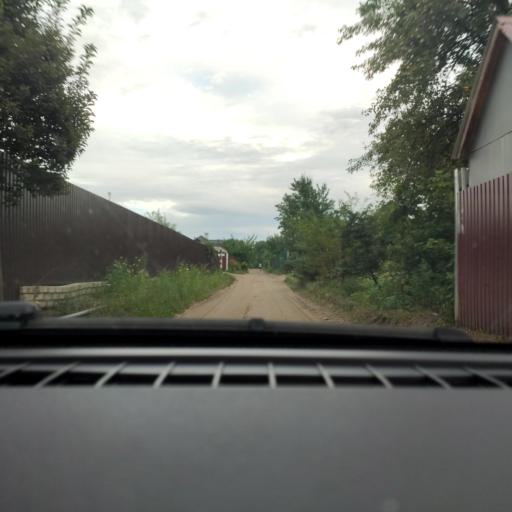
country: RU
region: Voronezj
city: Maslovka
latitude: 51.5223
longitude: 39.2337
